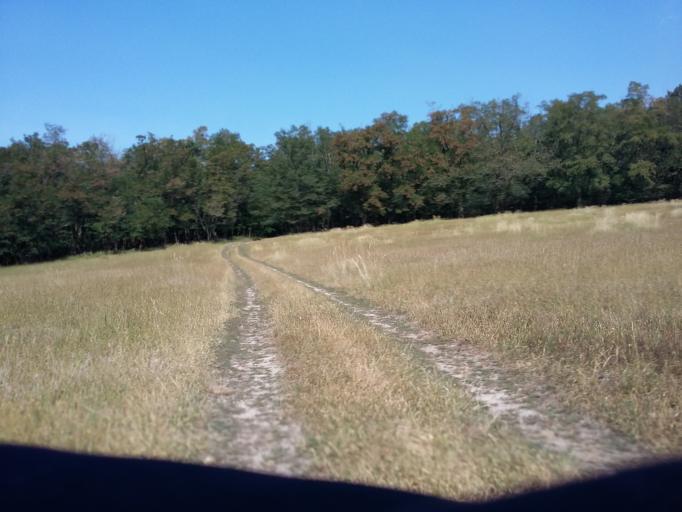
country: SK
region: Bratislavsky
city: Stupava
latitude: 48.3097
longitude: 17.0359
